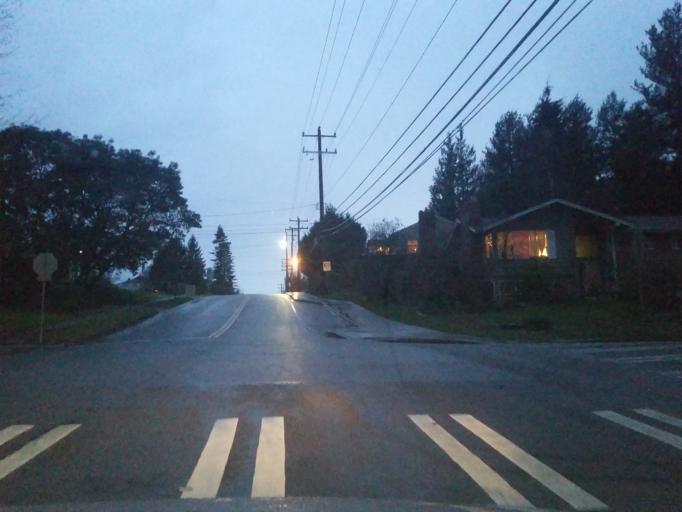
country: US
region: Washington
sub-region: King County
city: Shoreline
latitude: 47.7485
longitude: -122.3184
